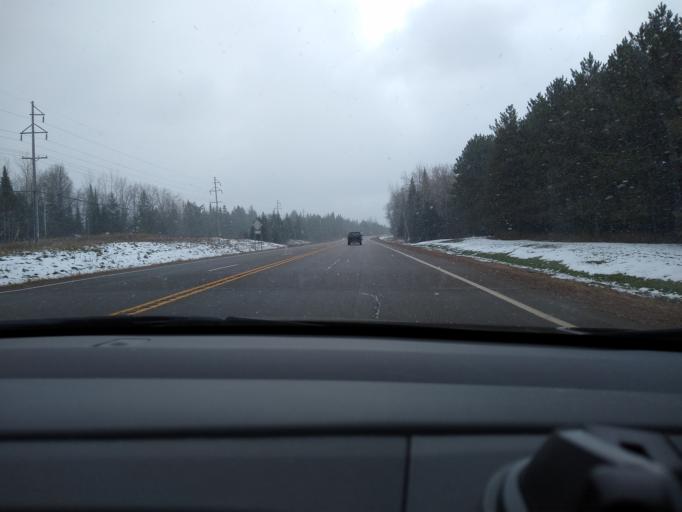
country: US
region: Michigan
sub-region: Dickinson County
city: Iron Mountain
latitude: 46.0371
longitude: -88.0603
